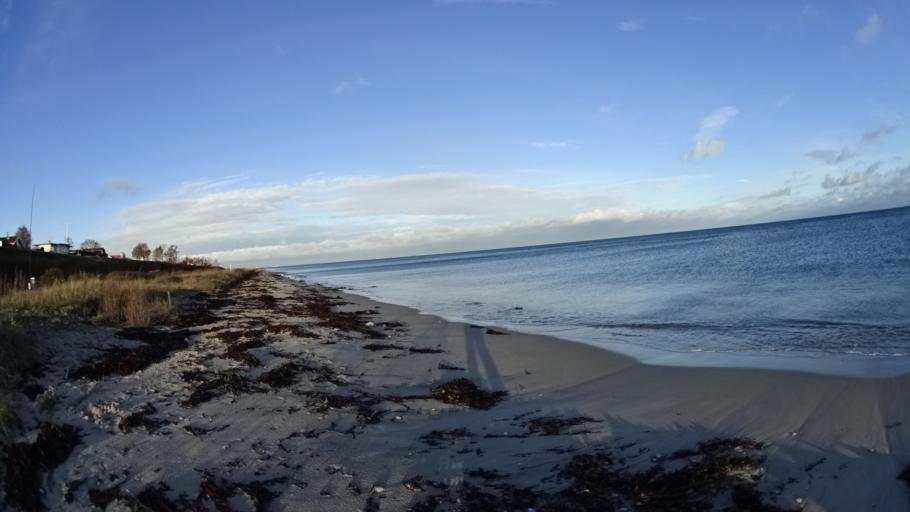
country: DK
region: Central Jutland
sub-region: Arhus Kommune
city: Beder
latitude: 56.0351
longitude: 10.2697
